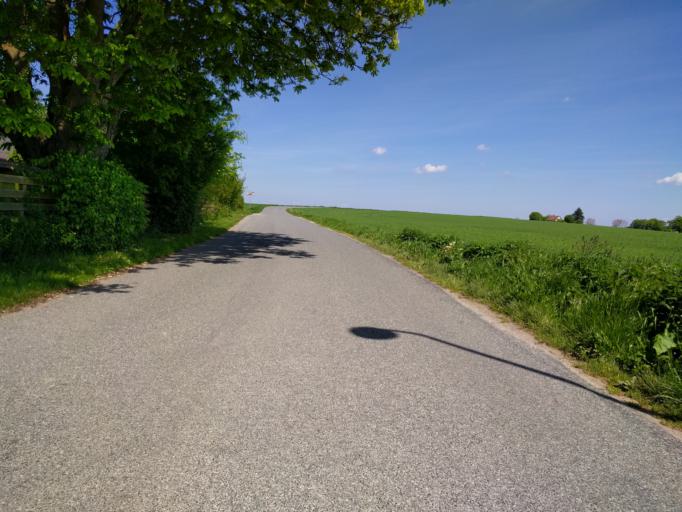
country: DK
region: Zealand
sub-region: Guldborgsund Kommune
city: Nykobing Falster
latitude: 54.7400
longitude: 12.0123
